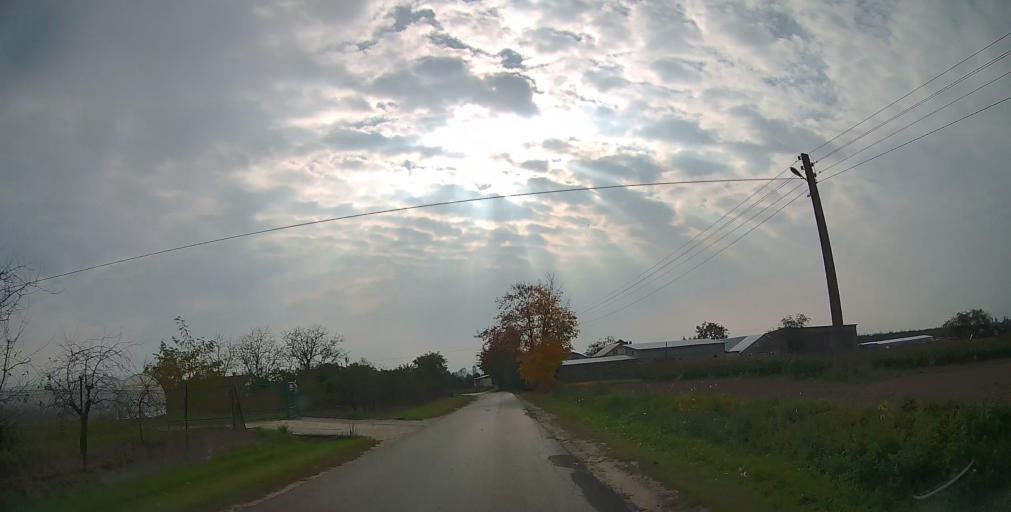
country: PL
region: Masovian Voivodeship
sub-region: Powiat grojecki
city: Mogielnica
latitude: 51.6465
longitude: 20.7341
